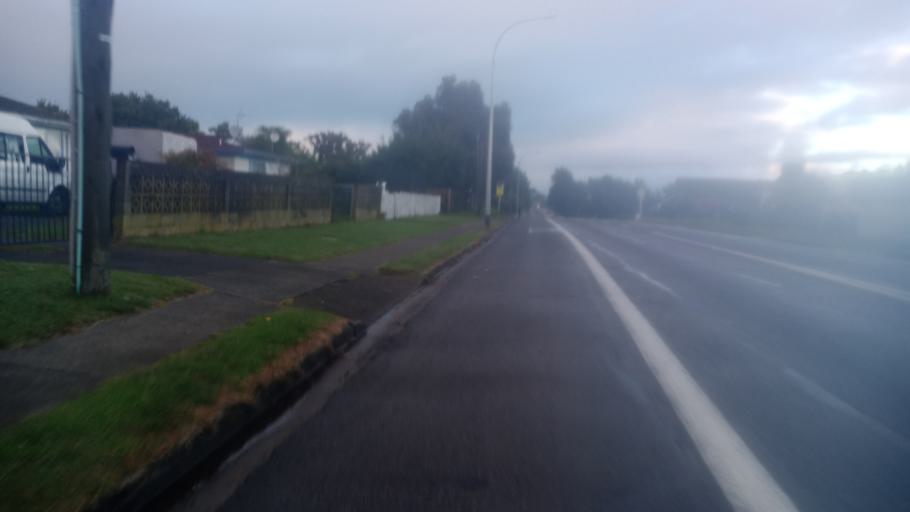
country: NZ
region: Gisborne
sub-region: Gisborne District
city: Gisborne
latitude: -38.6444
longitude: 178.0014
